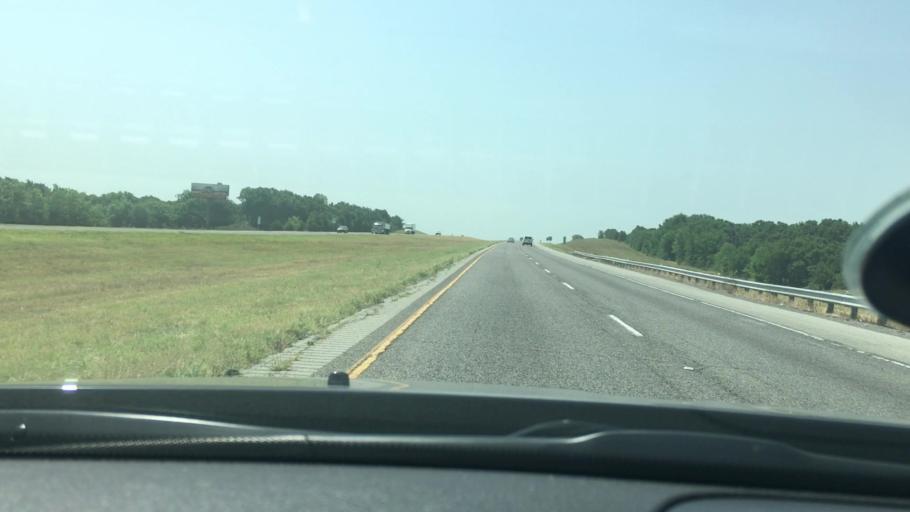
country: US
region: Oklahoma
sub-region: Garvin County
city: Wynnewood
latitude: 34.5821
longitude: -97.2026
